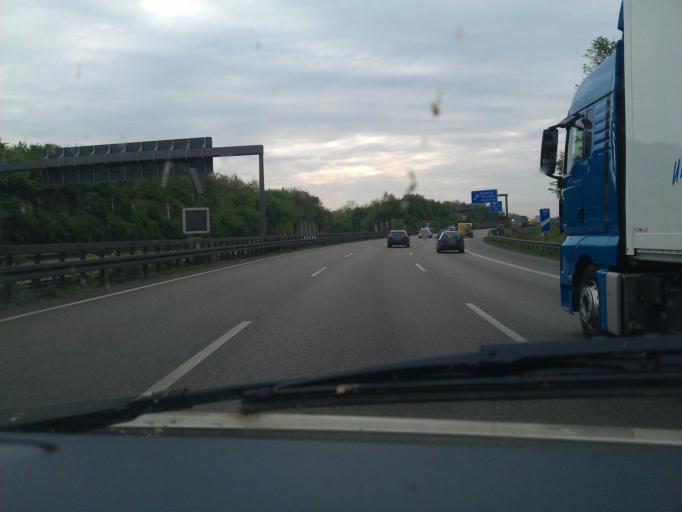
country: DE
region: North Rhine-Westphalia
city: Meiderich
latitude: 51.4863
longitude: 6.7857
